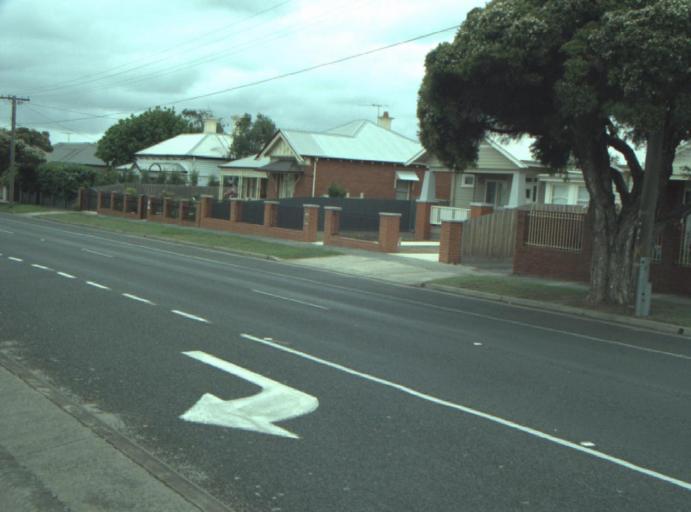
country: AU
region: Victoria
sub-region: Greater Geelong
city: East Geelong
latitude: -38.1563
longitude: 144.3682
